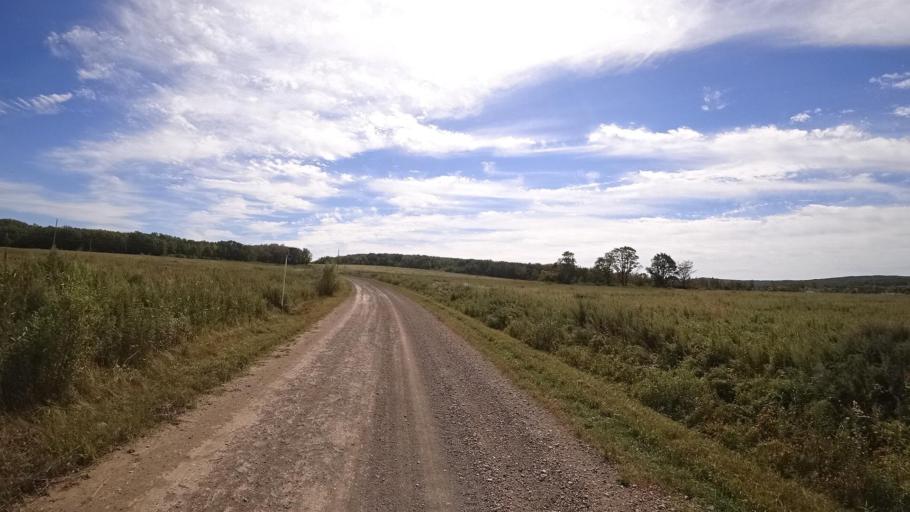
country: RU
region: Primorskiy
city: Yakovlevka
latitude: 44.7131
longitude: 133.6203
